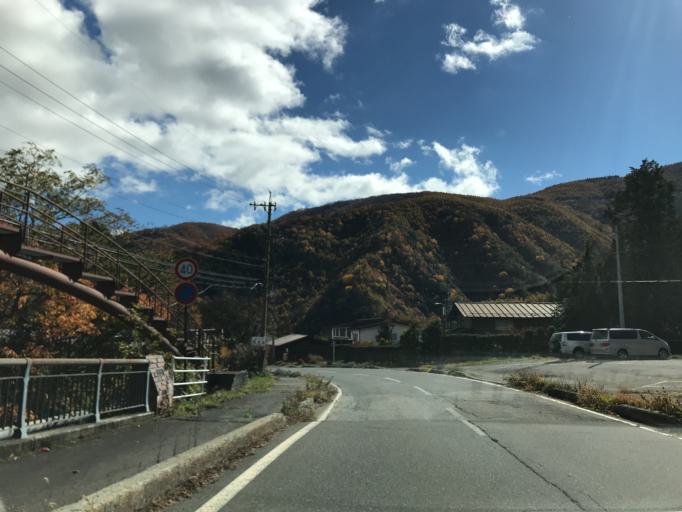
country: JP
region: Nagano
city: Toyoshina
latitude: 36.1248
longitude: 137.6519
